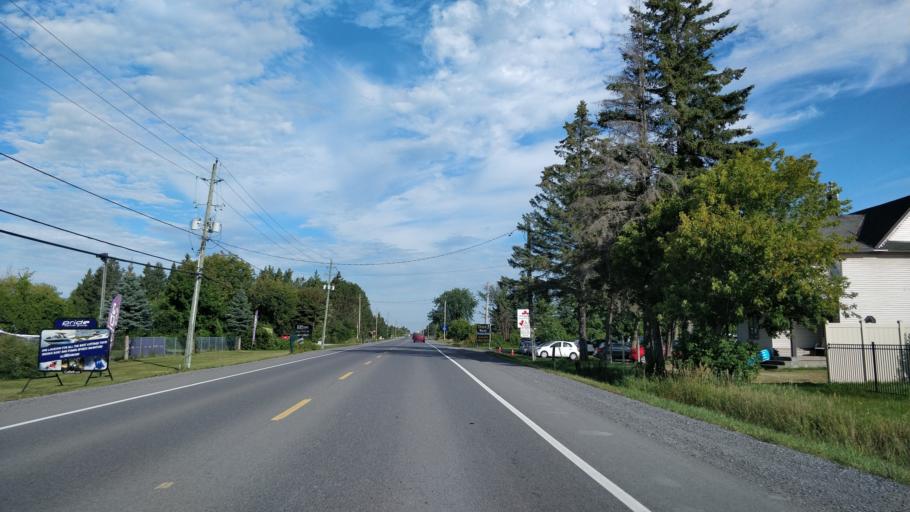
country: CA
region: Ontario
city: Bells Corners
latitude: 45.3068
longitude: -75.9889
